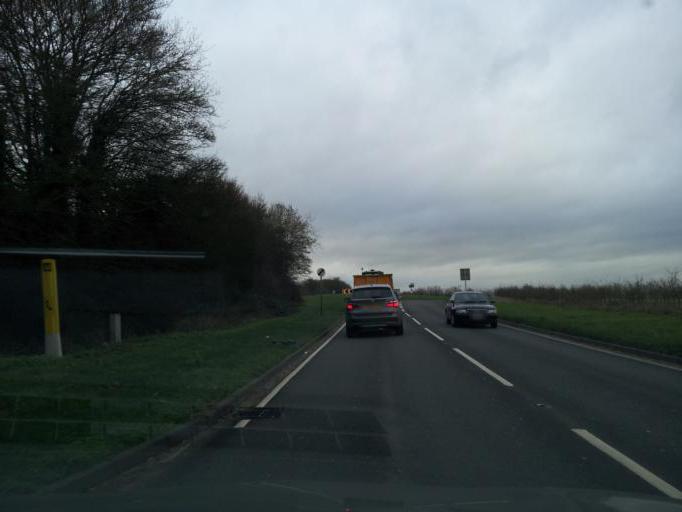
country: GB
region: England
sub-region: Norfolk
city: Long Stratton
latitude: 52.4361
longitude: 1.2103
